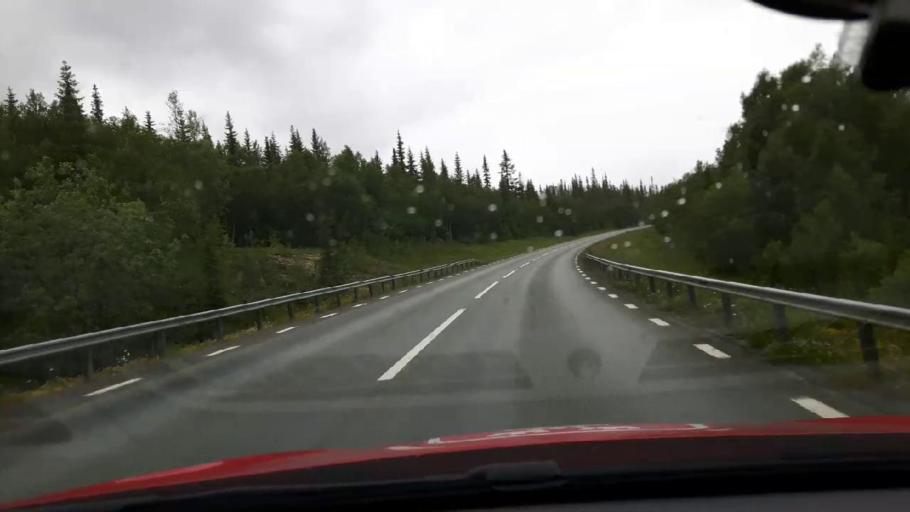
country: NO
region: Nord-Trondelag
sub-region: Meraker
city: Meraker
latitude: 63.2574
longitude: 12.1783
